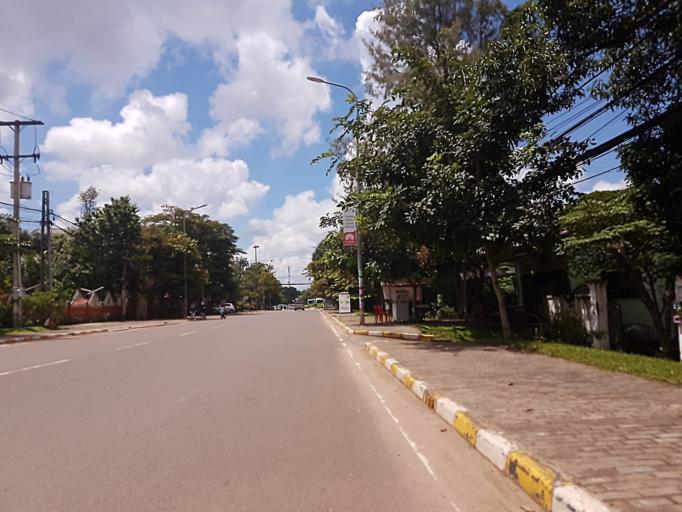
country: LA
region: Vientiane
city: Vientiane
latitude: 17.9725
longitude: 102.6225
